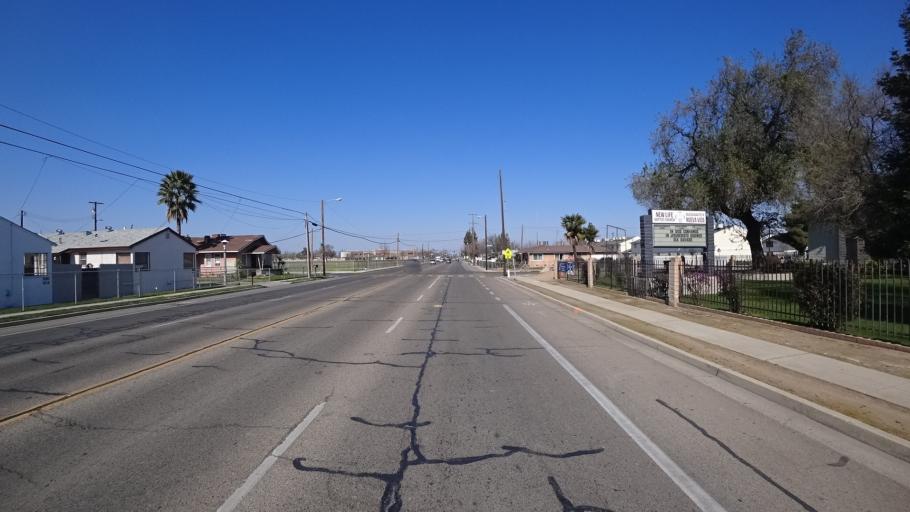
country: US
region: California
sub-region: Fresno County
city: Fresno
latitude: 36.7228
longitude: -119.7547
